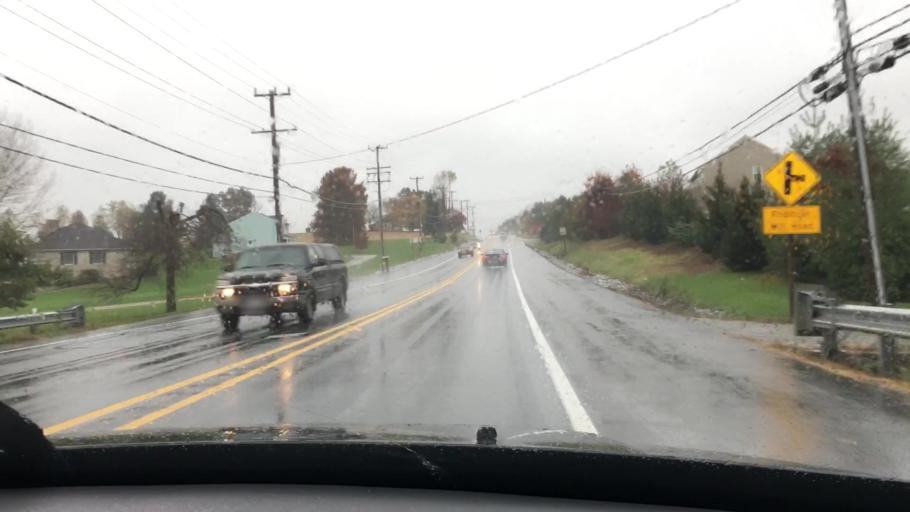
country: US
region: Maryland
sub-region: Carroll County
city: Manchester
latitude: 39.6769
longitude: -76.8918
